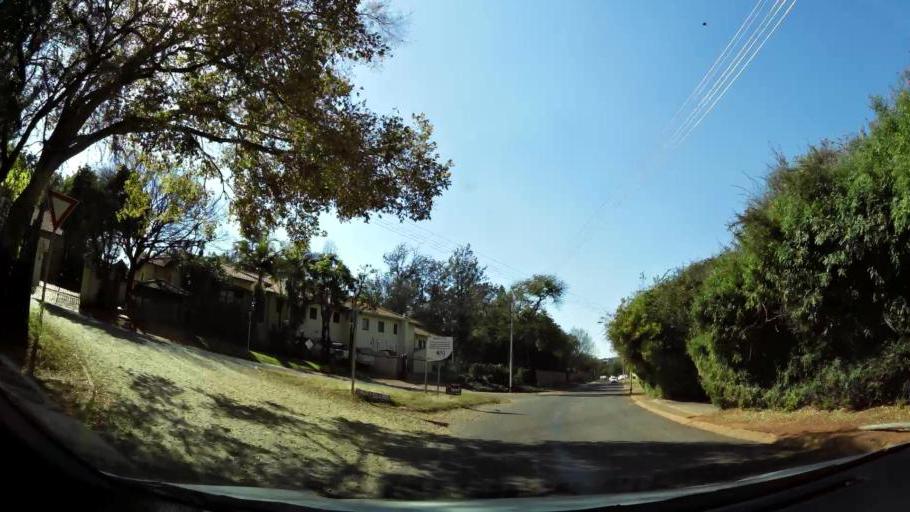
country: ZA
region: Gauteng
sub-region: City of Tshwane Metropolitan Municipality
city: Pretoria
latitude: -25.7603
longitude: 28.2700
